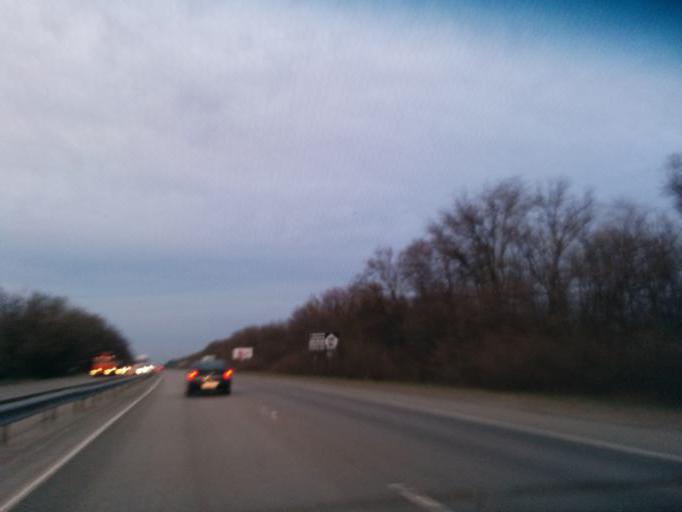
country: RU
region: Rostov
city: Grushevskaya
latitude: 47.4003
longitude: 39.9590
